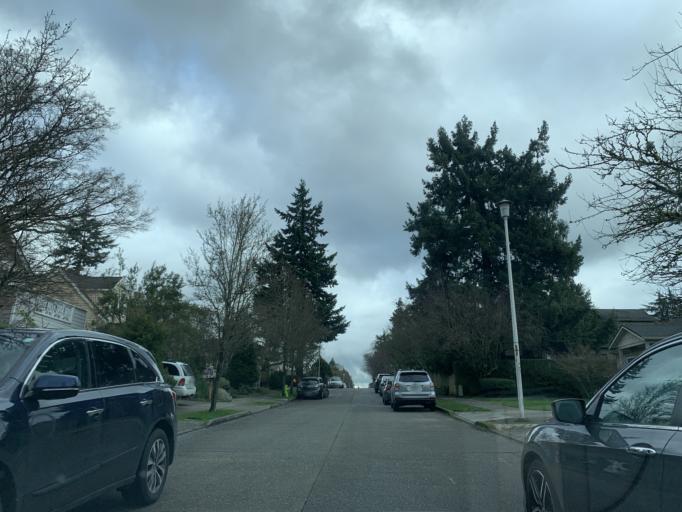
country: US
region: Washington
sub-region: King County
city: Yarrow Point
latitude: 47.6721
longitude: -122.2656
